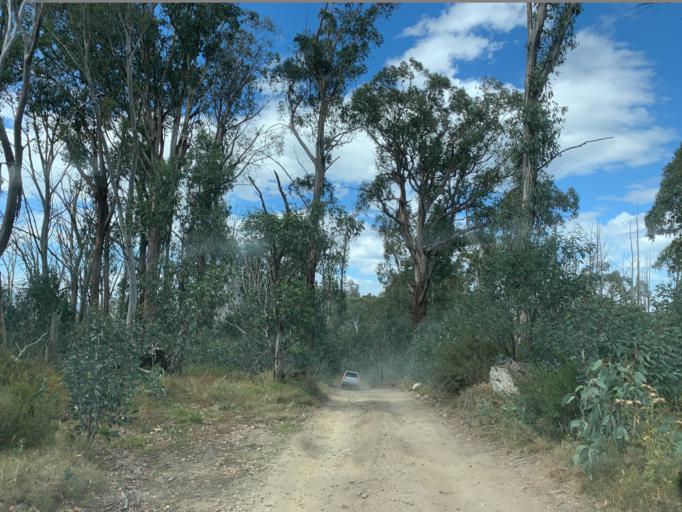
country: AU
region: Victoria
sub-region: Mansfield
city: Mansfield
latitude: -37.1029
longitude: 146.5396
